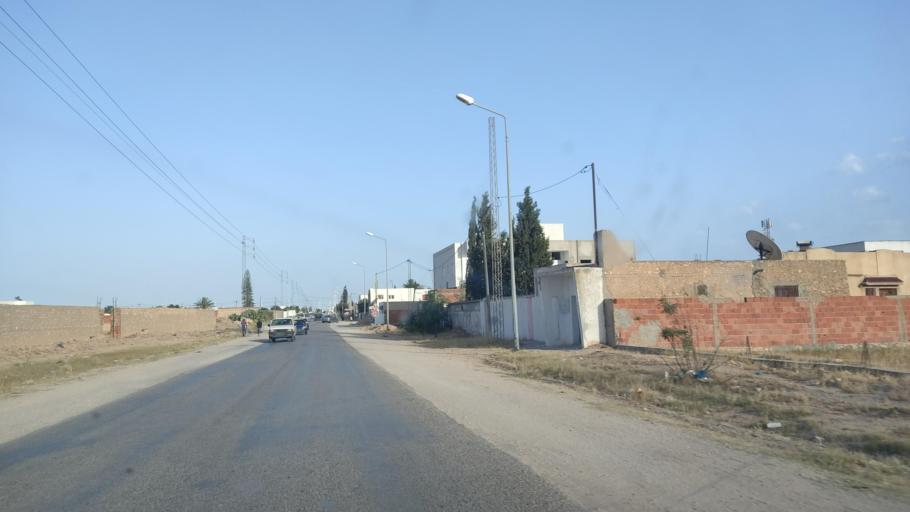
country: TN
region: Safaqis
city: Sfax
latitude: 34.8000
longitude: 10.6746
